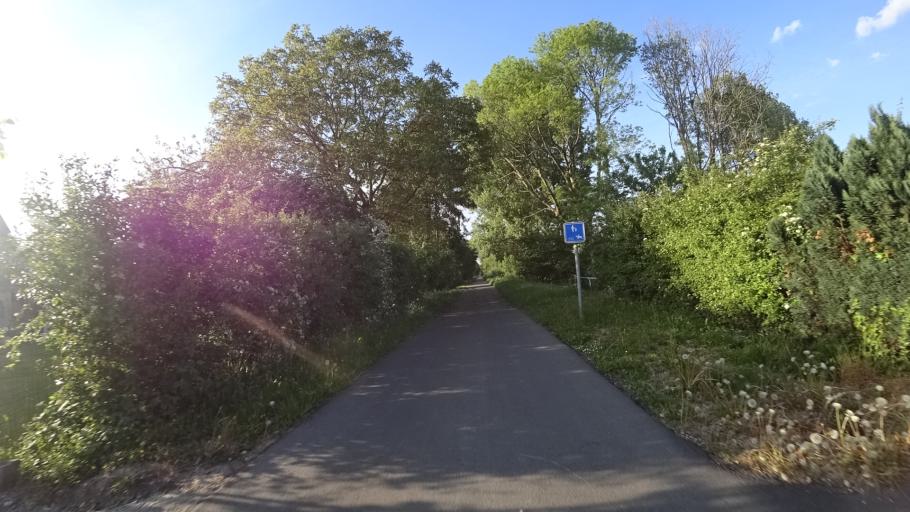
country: BE
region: Wallonia
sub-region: Province de Namur
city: Eghezee
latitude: 50.5529
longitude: 4.9039
